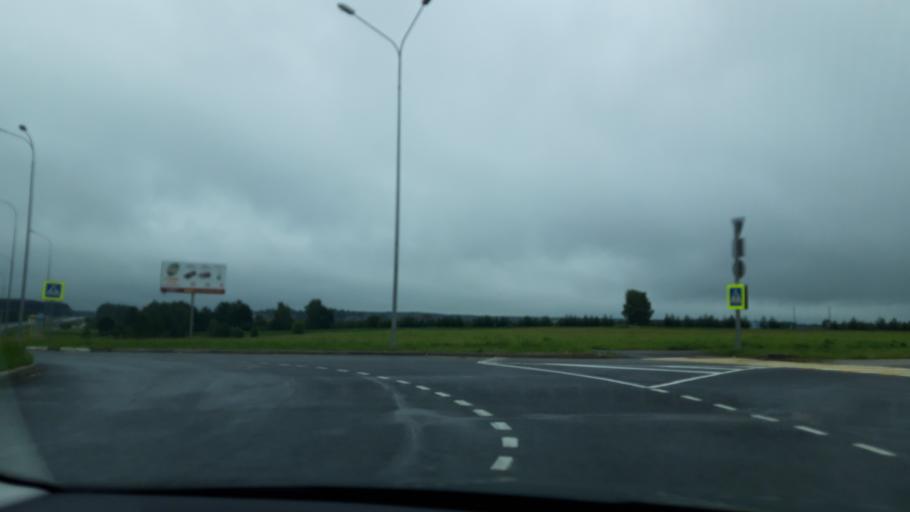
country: RU
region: Tverskaya
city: Zavidovo
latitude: 56.5779
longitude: 36.5199
